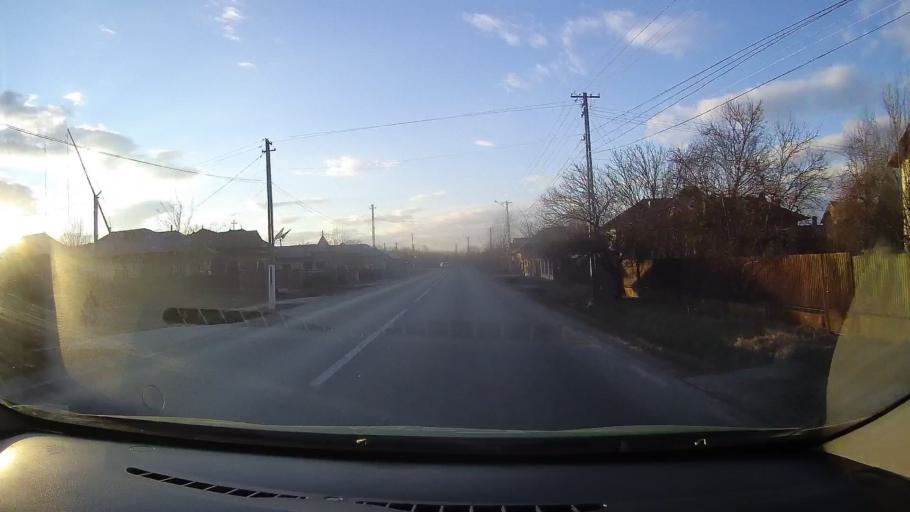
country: RO
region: Dambovita
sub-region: Comuna Gura Ocnitei
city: Adanca
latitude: 44.9093
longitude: 25.6185
